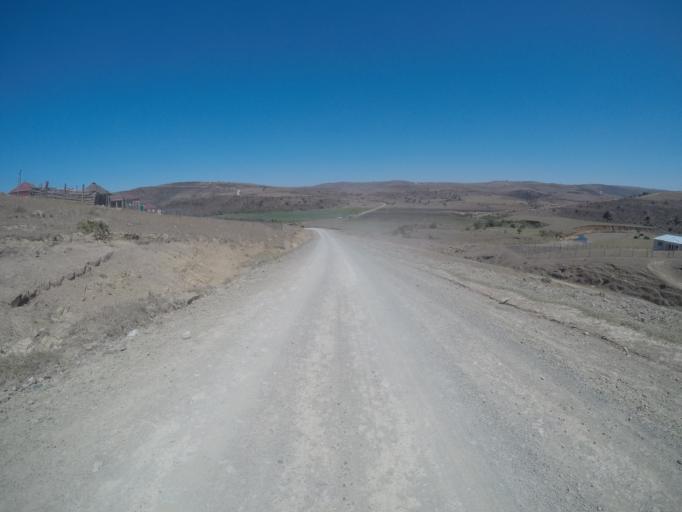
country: ZA
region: Eastern Cape
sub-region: OR Tambo District Municipality
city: Mthatha
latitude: -31.8658
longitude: 28.8721
